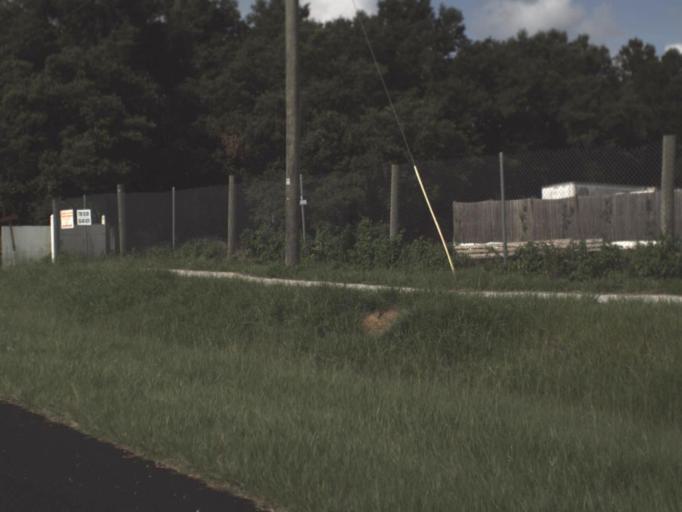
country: US
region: Florida
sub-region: Pasco County
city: Dade City North
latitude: 28.4195
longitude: -82.1907
